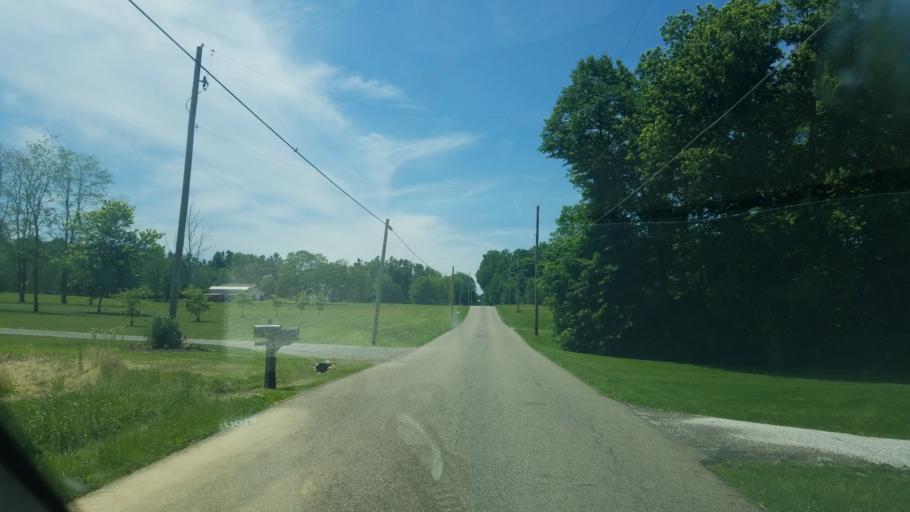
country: US
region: Ohio
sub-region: Stark County
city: Alliance
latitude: 40.8574
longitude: -81.0915
